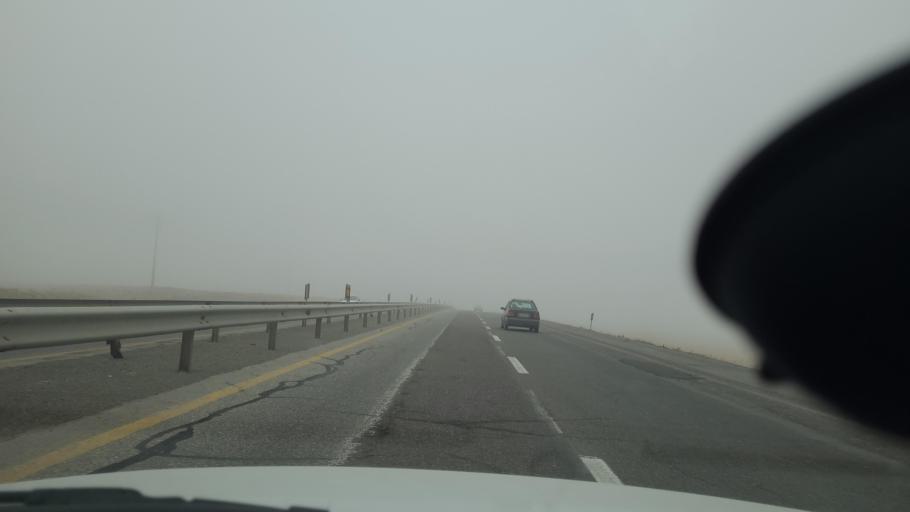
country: IR
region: Razavi Khorasan
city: Fariman
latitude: 35.7880
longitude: 59.7412
